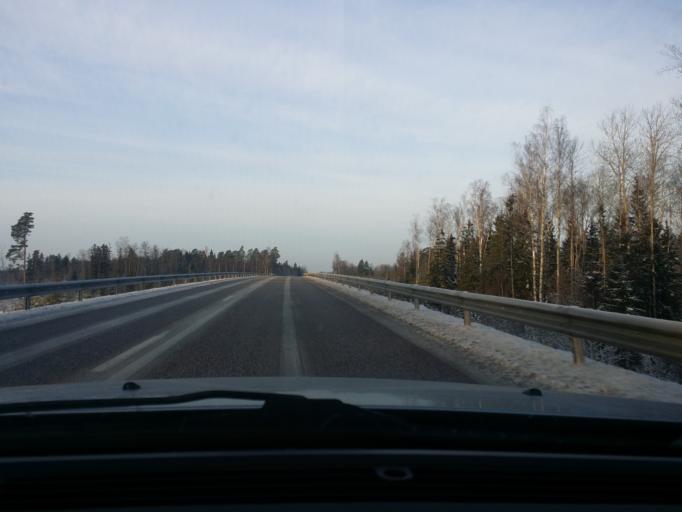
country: SE
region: OErebro
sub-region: Lindesbergs Kommun
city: Frovi
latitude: 59.4687
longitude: 15.4084
